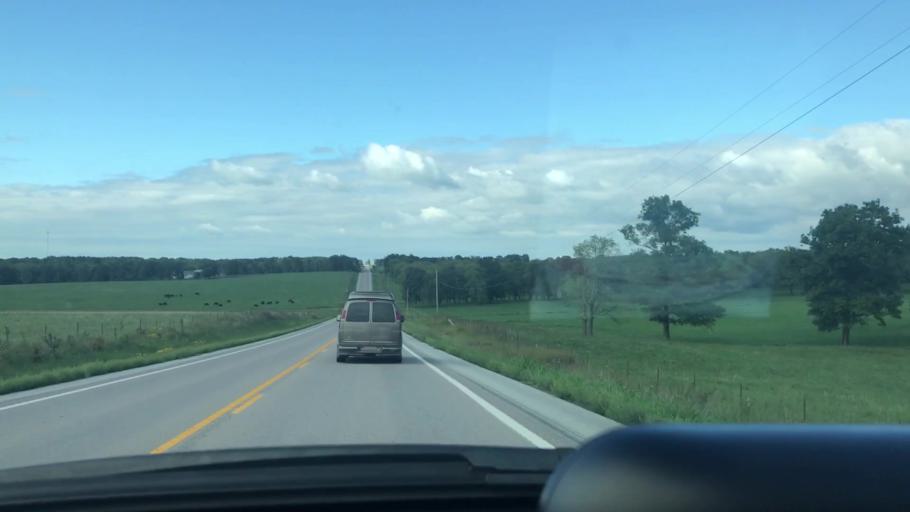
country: US
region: Missouri
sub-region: Hickory County
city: Hermitage
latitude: 37.9670
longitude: -93.2061
